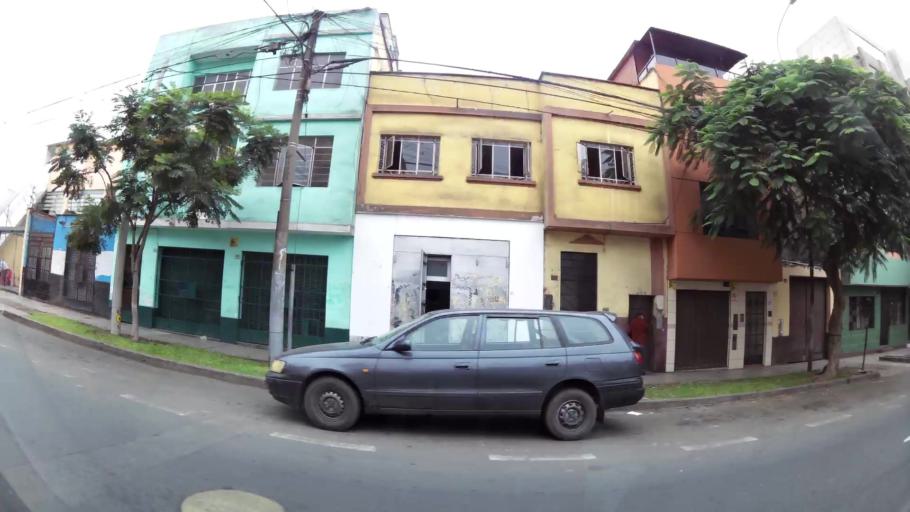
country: PE
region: Lima
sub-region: Lima
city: San Isidro
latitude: -12.0888
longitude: -77.0314
